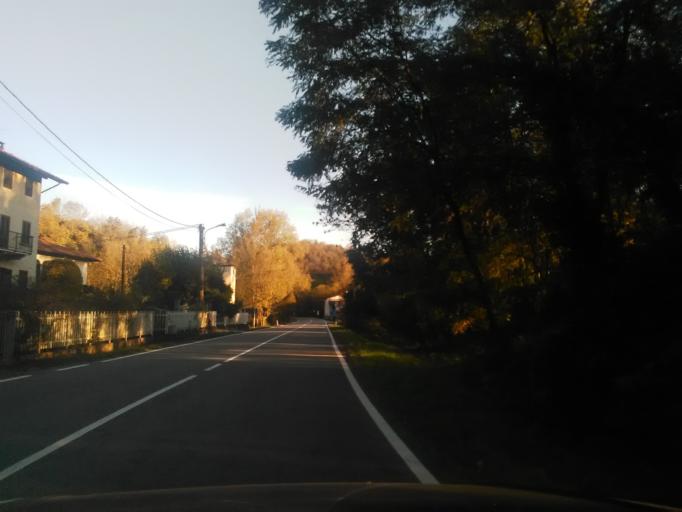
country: IT
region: Piedmont
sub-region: Provincia di Biella
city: Villa del Bosco
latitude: 45.6253
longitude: 8.2802
